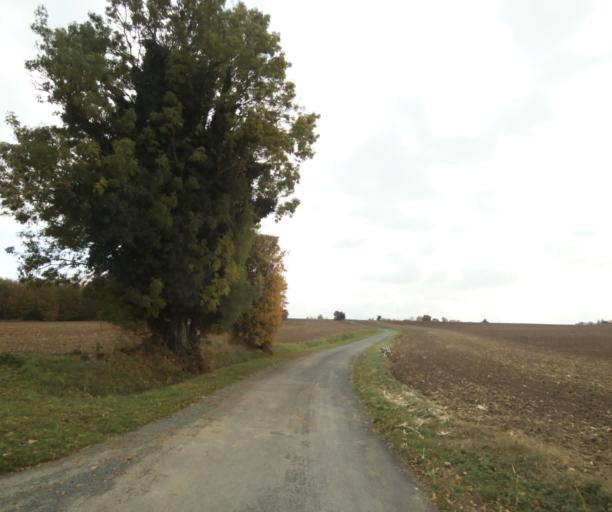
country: FR
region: Poitou-Charentes
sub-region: Departement de la Charente-Maritime
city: Saint-Georges-des-Coteaux
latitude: 45.7755
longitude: -0.7115
